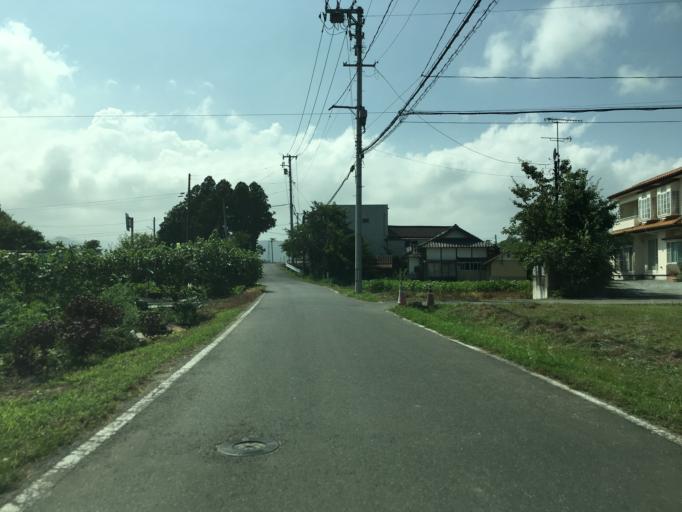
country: JP
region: Miyagi
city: Marumori
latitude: 37.8333
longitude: 140.9195
